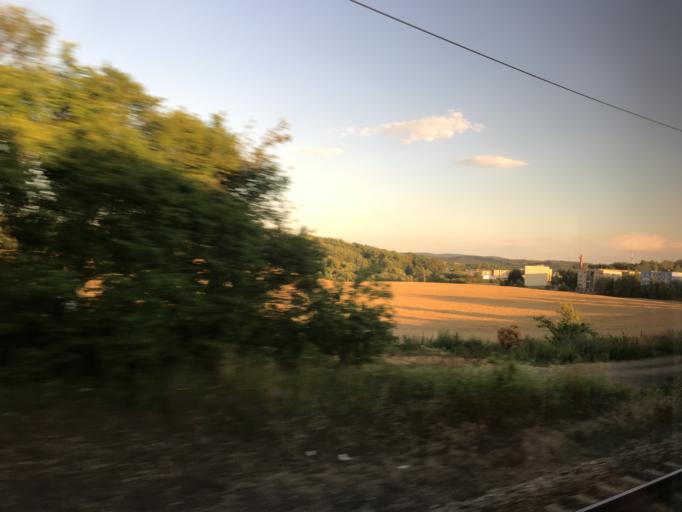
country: CZ
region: Central Bohemia
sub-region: Okres Benesov
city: Benesov
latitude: 49.7945
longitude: 14.6990
